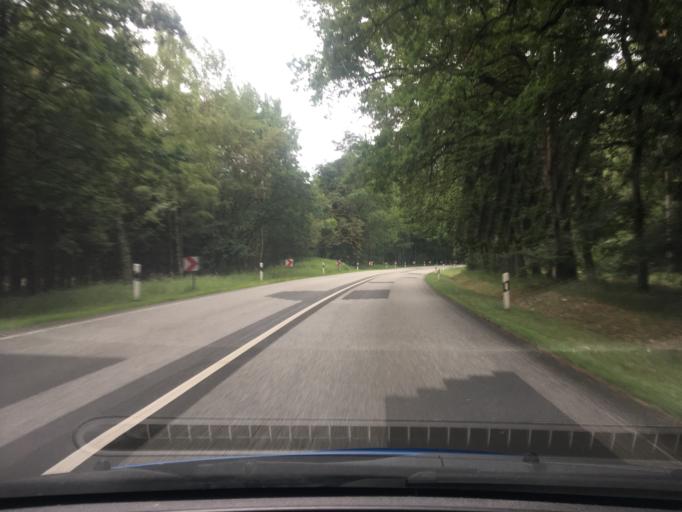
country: DE
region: Mecklenburg-Vorpommern
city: Stralendorf
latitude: 53.5191
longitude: 11.3002
